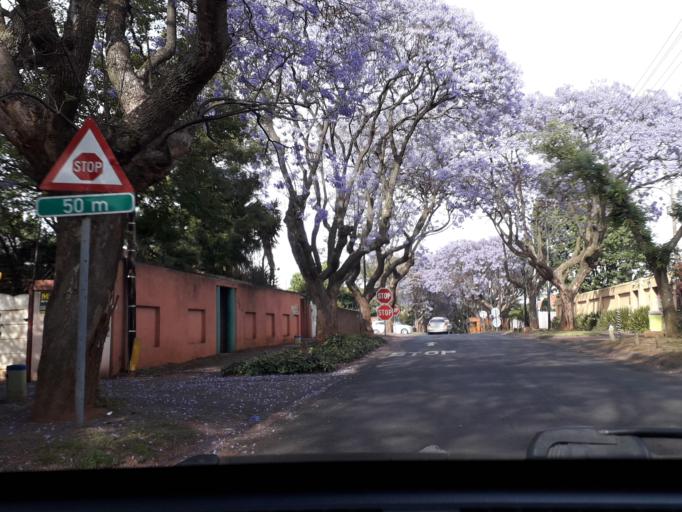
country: ZA
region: Gauteng
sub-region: City of Johannesburg Metropolitan Municipality
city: Johannesburg
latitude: -26.1452
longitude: 28.0908
